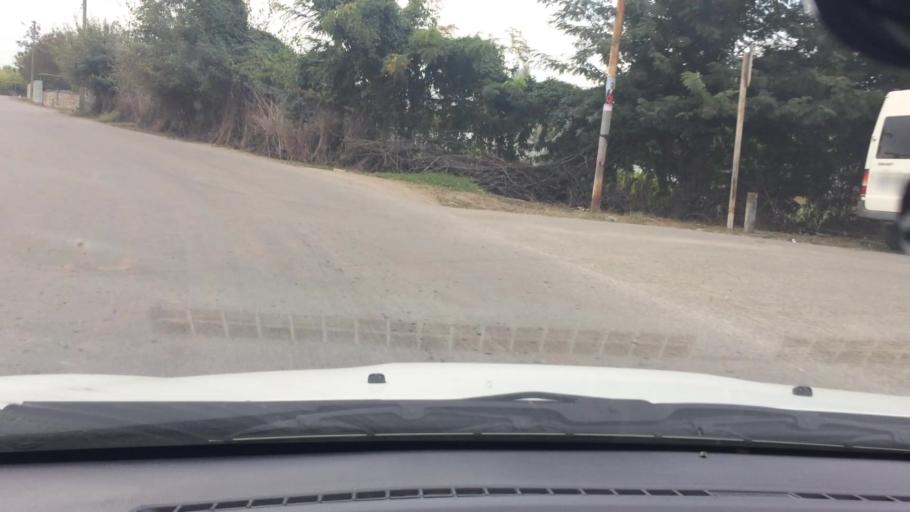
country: AM
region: Tavush
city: Berdavan
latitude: 41.3519
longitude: 44.9697
